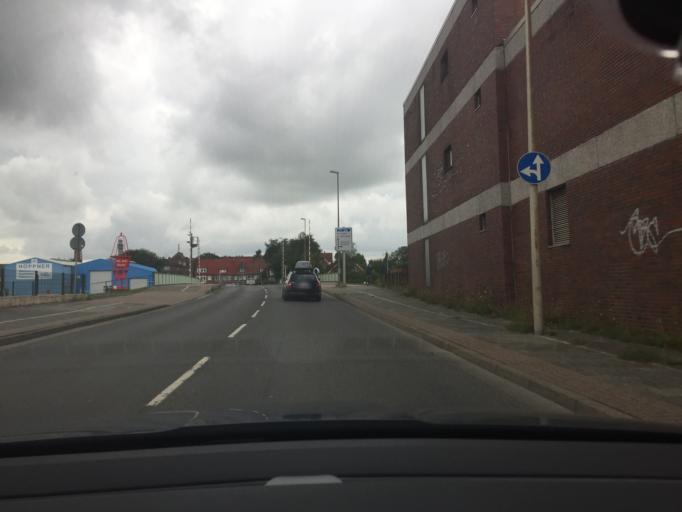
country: DE
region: Lower Saxony
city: Emden
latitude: 53.3602
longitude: 7.2054
